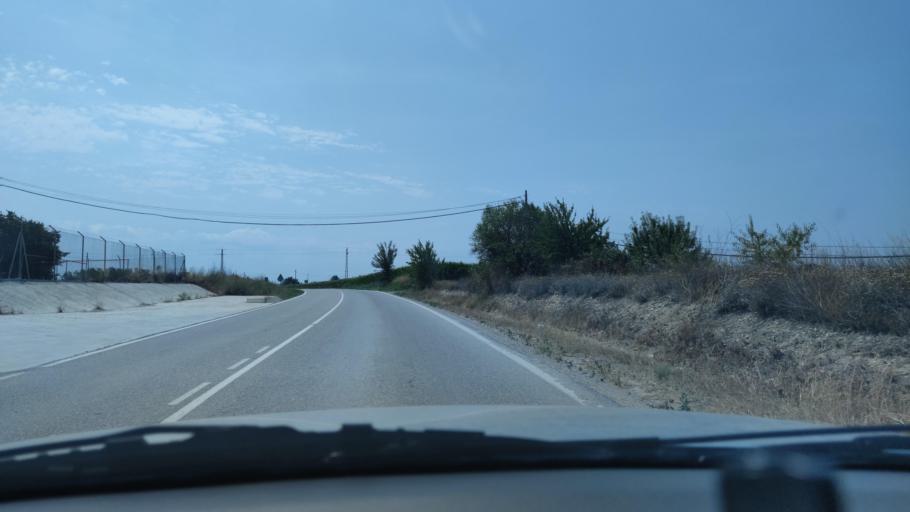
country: ES
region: Catalonia
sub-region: Provincia de Lleida
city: Bellpuig
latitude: 41.6408
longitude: 1.0011
